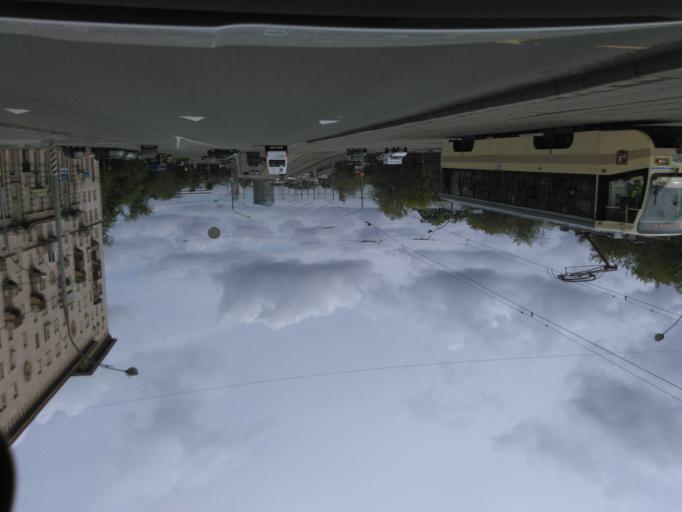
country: RU
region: Moscow
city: Taganskiy
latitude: 55.7304
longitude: 37.6590
